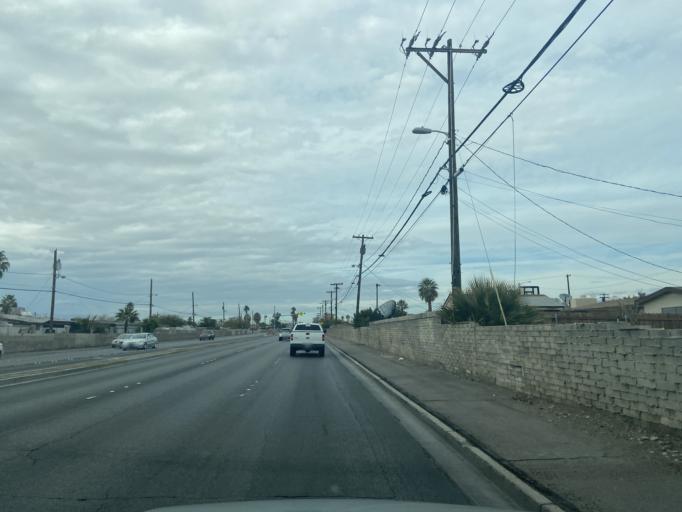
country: US
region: Nevada
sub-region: Clark County
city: Las Vegas
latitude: 36.1835
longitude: -115.1812
